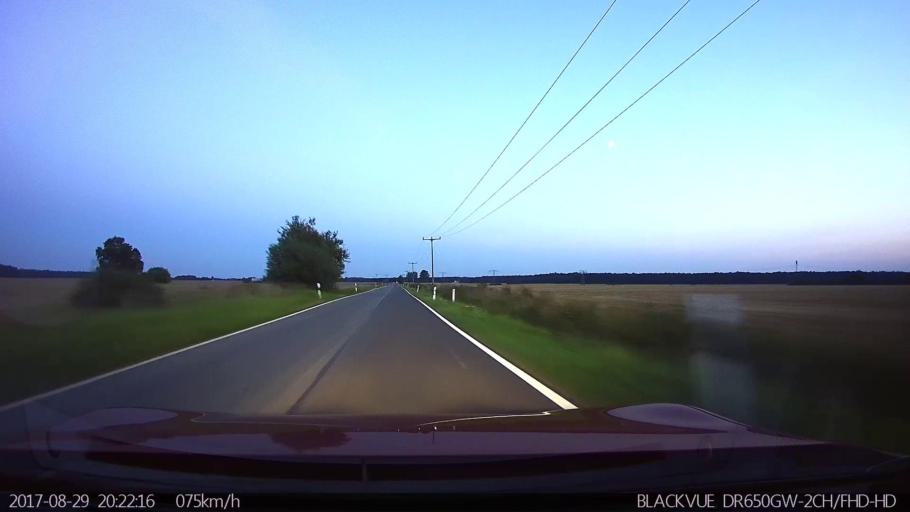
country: DE
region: Mecklenburg-Vorpommern
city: Velgast
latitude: 54.2406
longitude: 12.8236
